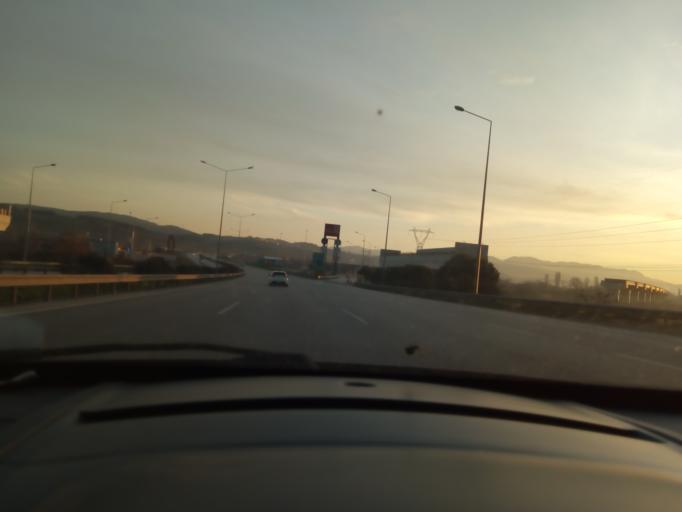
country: TR
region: Bursa
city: Niluefer
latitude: 40.2801
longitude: 28.9918
